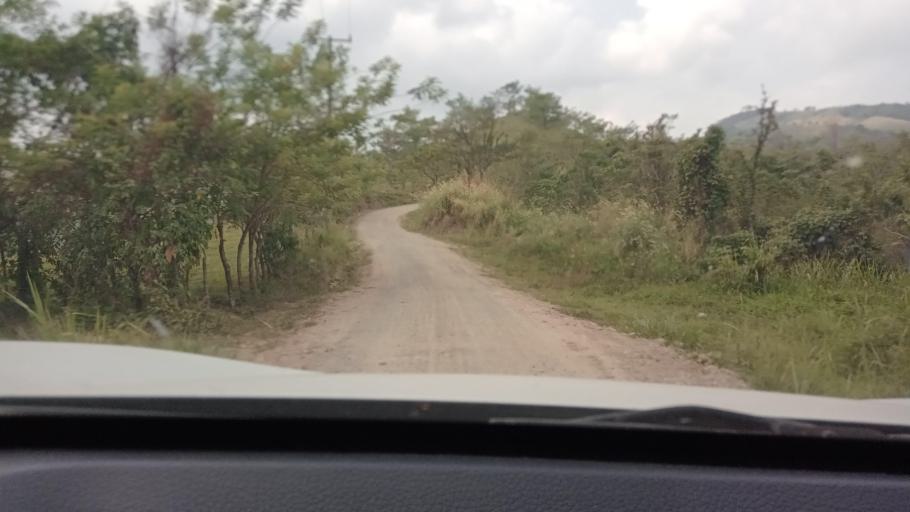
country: MX
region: Tabasco
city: Chontalpa
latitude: 17.4968
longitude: -93.6513
